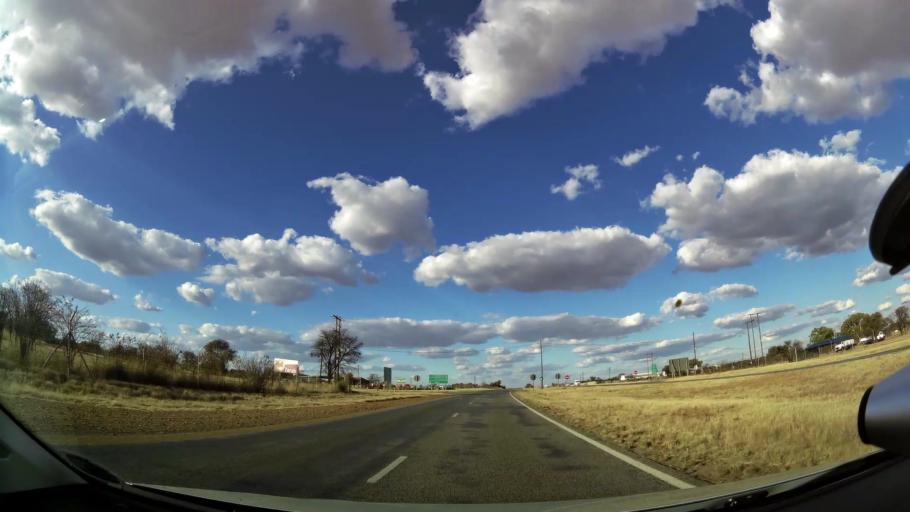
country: ZA
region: North-West
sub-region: Dr Kenneth Kaunda District Municipality
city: Stilfontein
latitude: -26.7895
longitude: 26.9211
